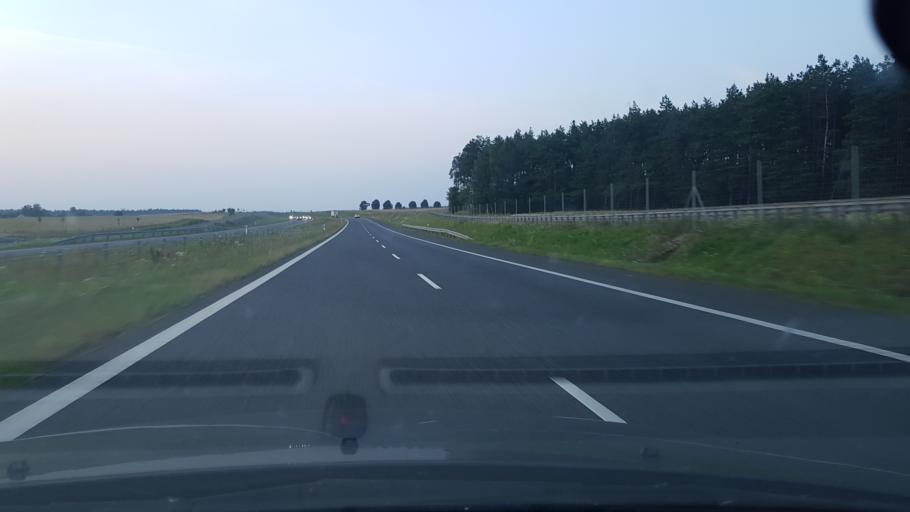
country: PL
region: Warmian-Masurian Voivodeship
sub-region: Powiat nidzicki
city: Nidzica
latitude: 53.4293
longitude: 20.3378
